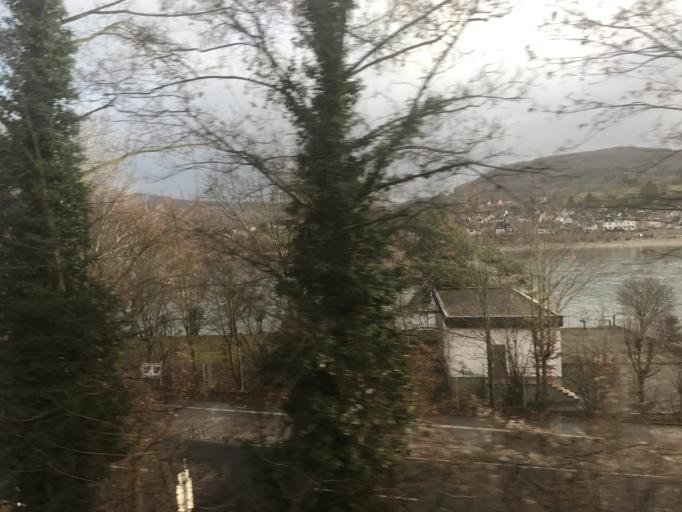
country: DE
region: Rheinland-Pfalz
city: Filsen
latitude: 50.2381
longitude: 7.5760
